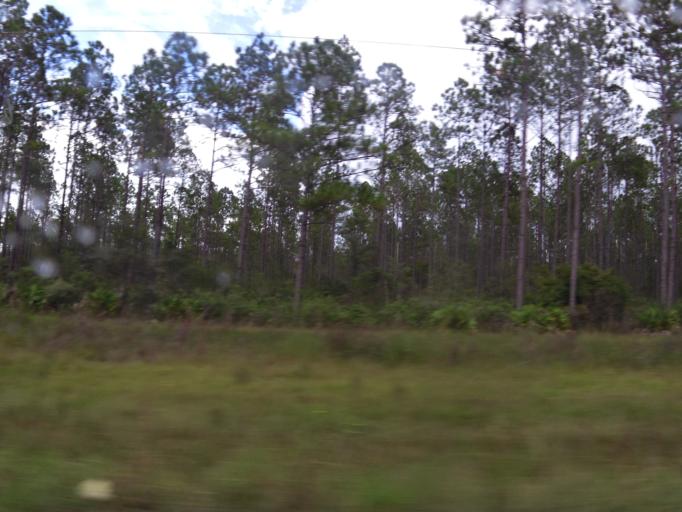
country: US
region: Florida
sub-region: Nassau County
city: Hilliard
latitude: 30.5829
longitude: -82.0466
